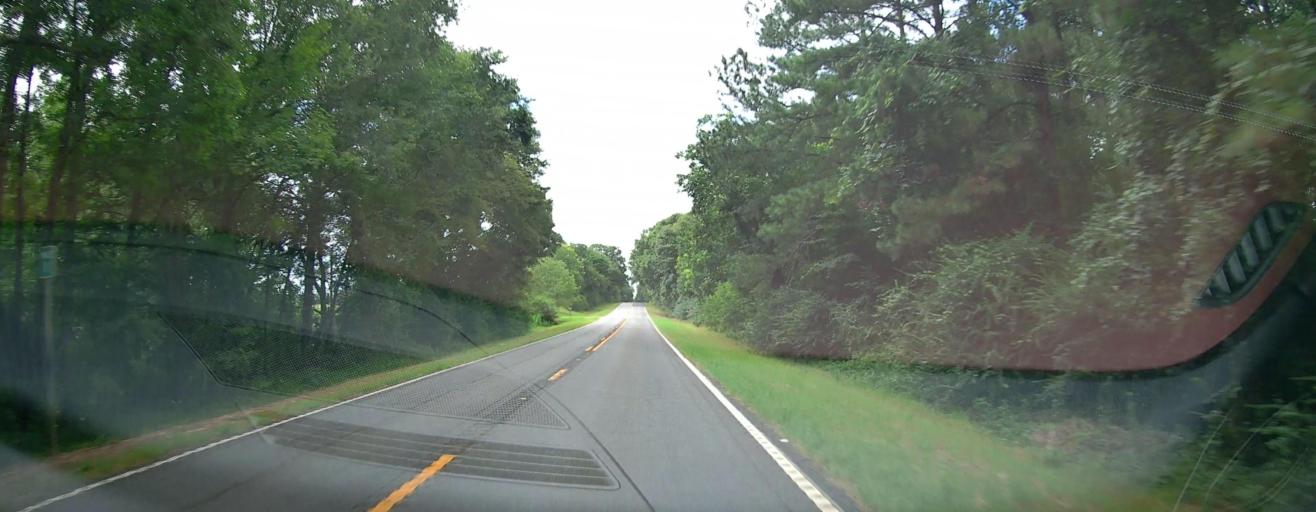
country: US
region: Georgia
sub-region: Dooly County
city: Unadilla
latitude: 32.2913
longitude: -83.8672
